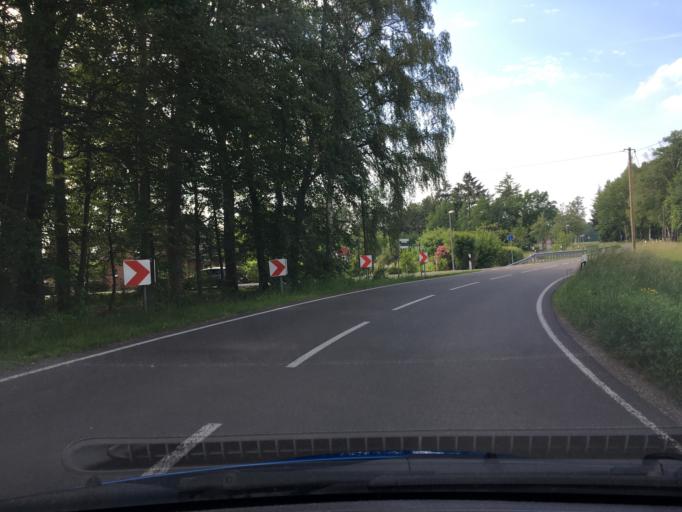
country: DE
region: Lower Saxony
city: Kalbe
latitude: 53.2806
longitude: 9.5639
